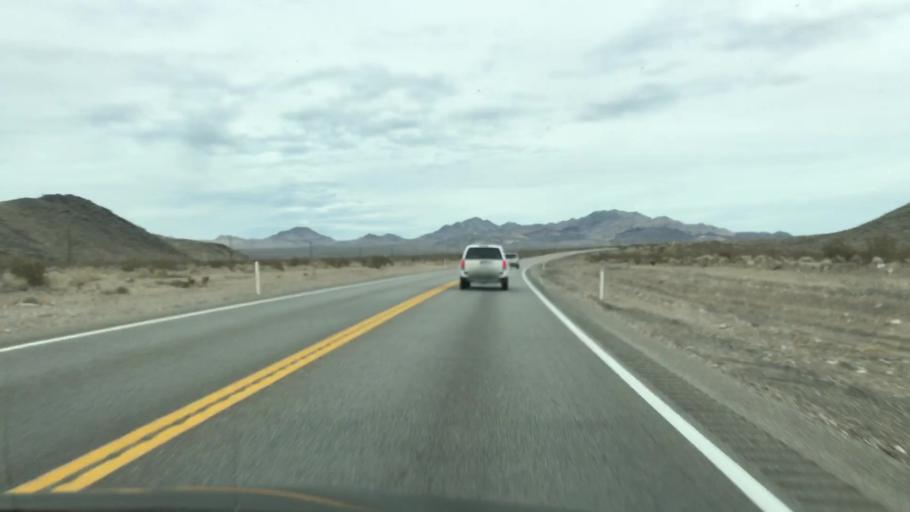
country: US
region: Nevada
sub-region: Nye County
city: Pahrump
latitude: 36.5850
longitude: -116.0601
